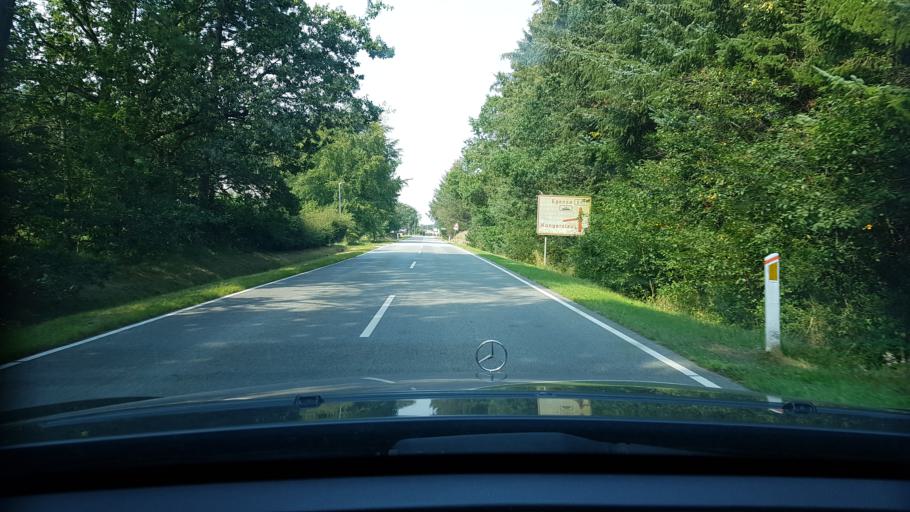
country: DK
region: North Denmark
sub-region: Alborg Kommune
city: Hals
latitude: 56.8995
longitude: 10.2575
